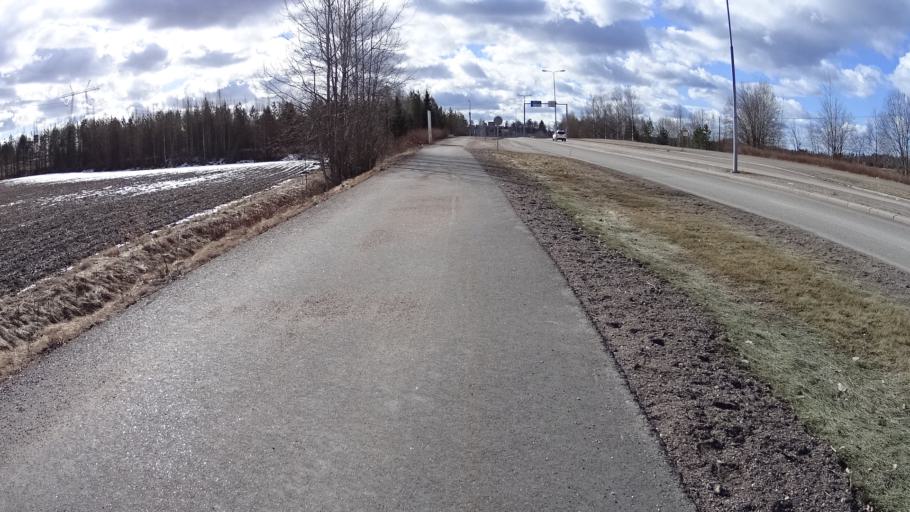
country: FI
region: Uusimaa
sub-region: Helsinki
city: Kauniainen
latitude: 60.2541
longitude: 24.7118
